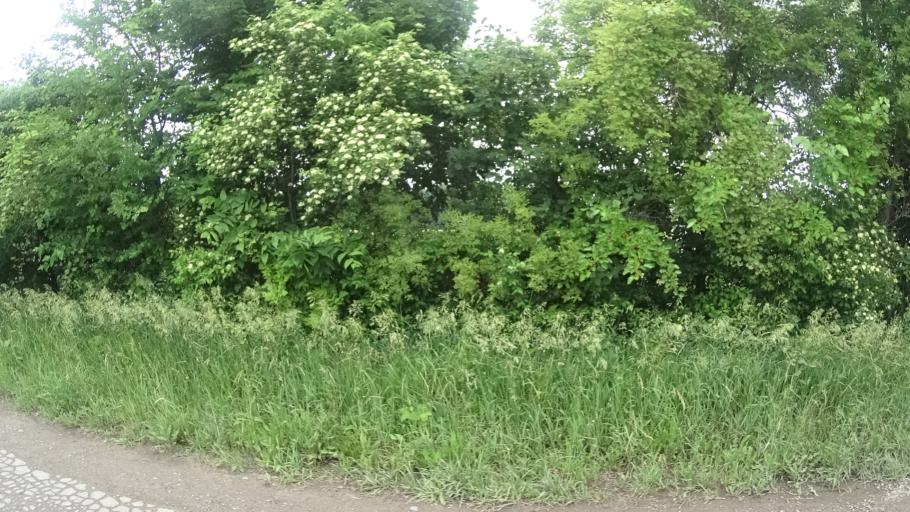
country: US
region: Ohio
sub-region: Huron County
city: Bellevue
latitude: 41.2909
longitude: -82.8042
